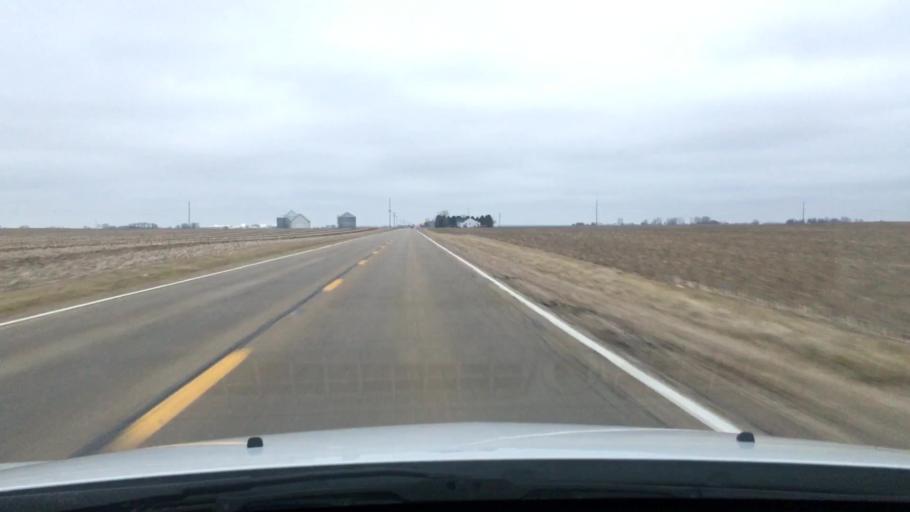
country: US
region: Illinois
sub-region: Bureau County
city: Ladd
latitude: 41.4355
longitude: -89.1268
